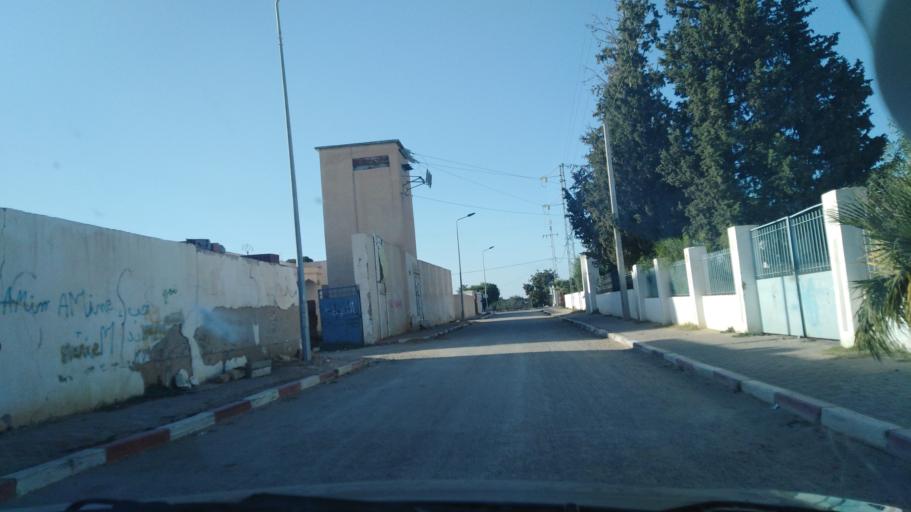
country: TN
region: Al Mahdiyah
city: Shurban
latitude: 34.9653
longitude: 10.3684
